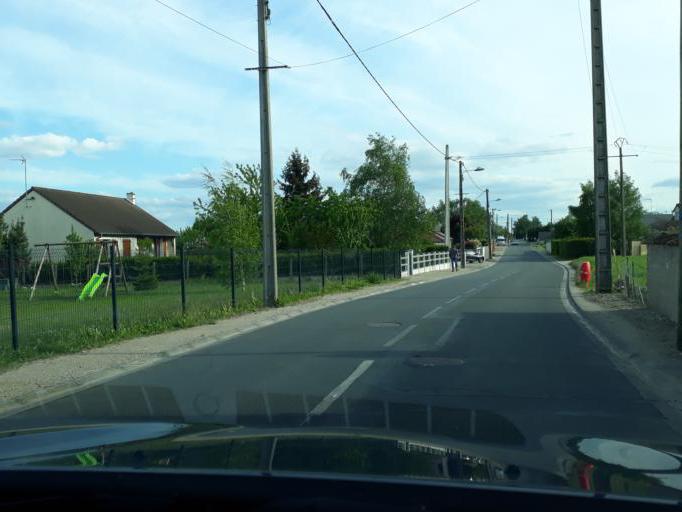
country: FR
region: Centre
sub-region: Departement du Loiret
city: Ingre
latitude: 47.9096
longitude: 1.8449
